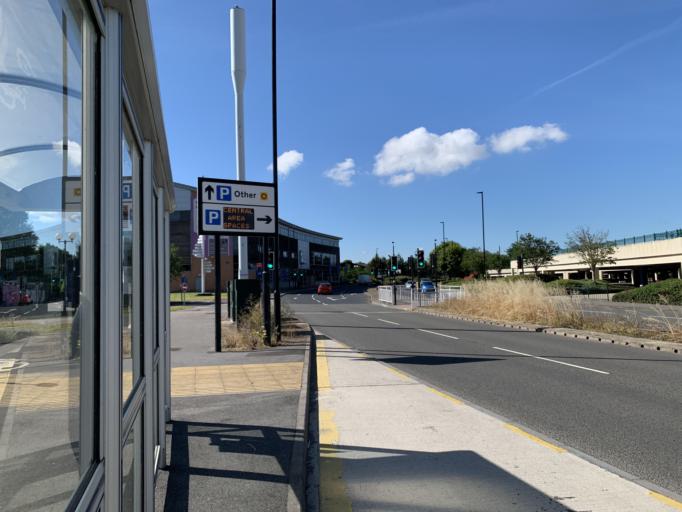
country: GB
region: England
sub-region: Rotherham
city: Catcliffe
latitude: 53.4149
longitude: -1.4057
